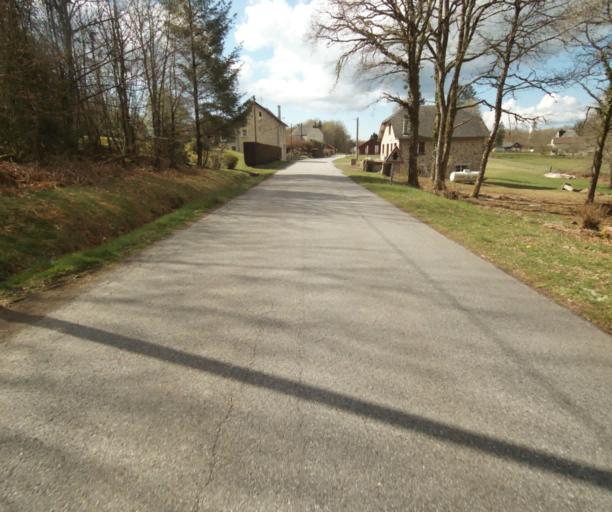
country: FR
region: Limousin
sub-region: Departement de la Correze
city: Argentat
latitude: 45.2269
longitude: 1.9336
